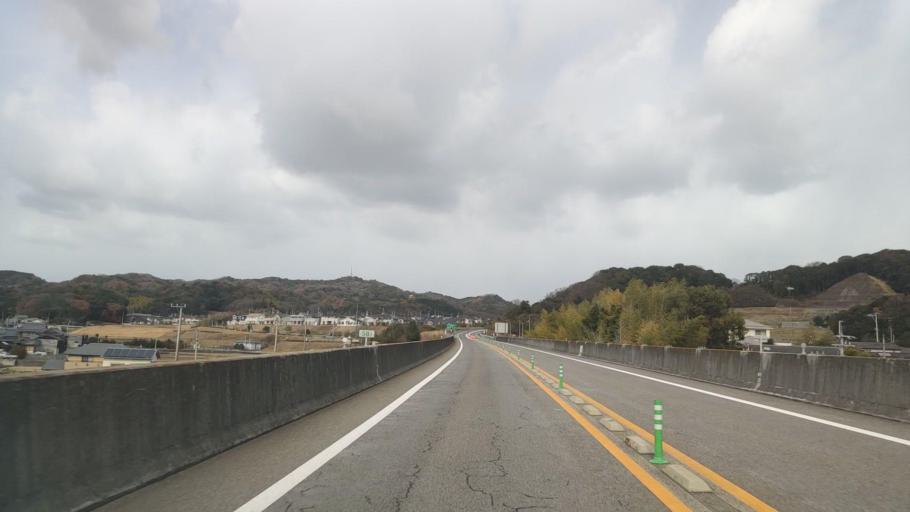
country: JP
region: Ehime
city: Hojo
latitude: 34.0632
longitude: 132.9731
